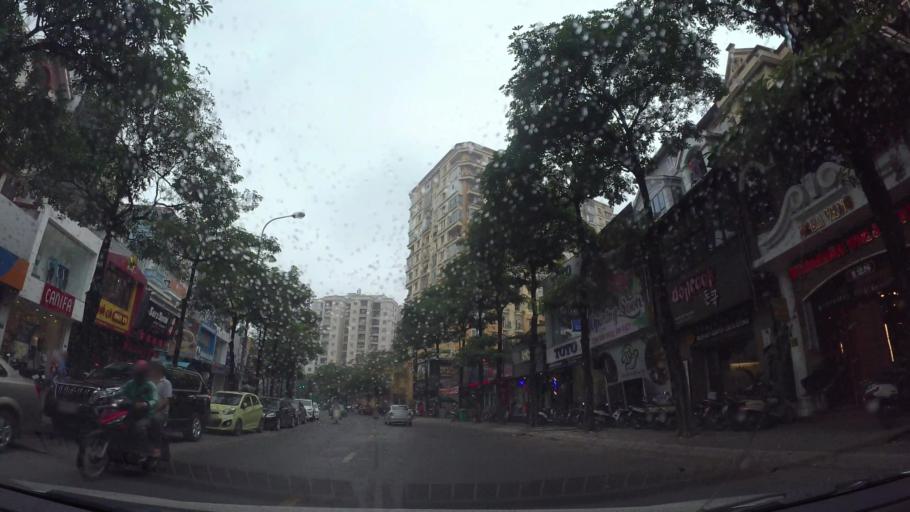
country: VN
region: Ha Noi
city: Cau Giay
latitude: 21.0169
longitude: 105.7994
